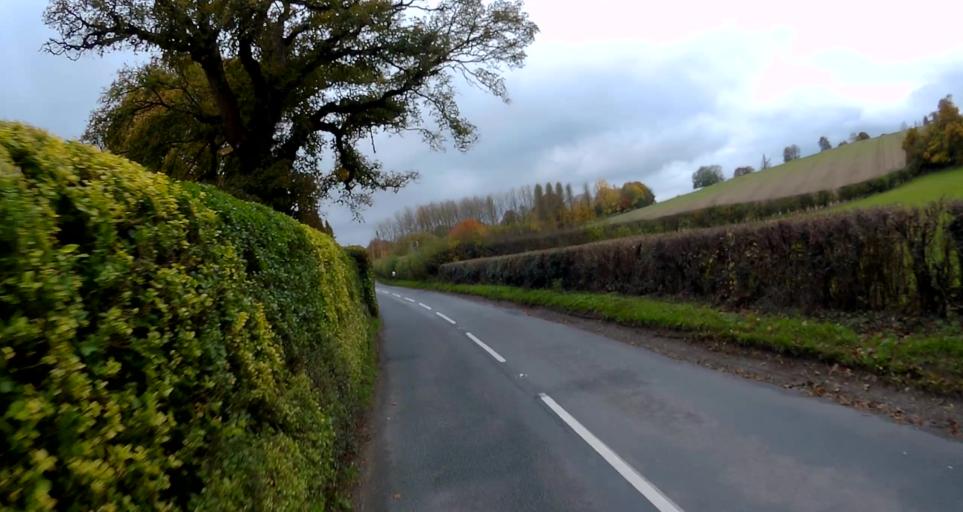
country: GB
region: England
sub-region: Hampshire
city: Basingstoke
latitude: 51.1811
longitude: -1.1275
